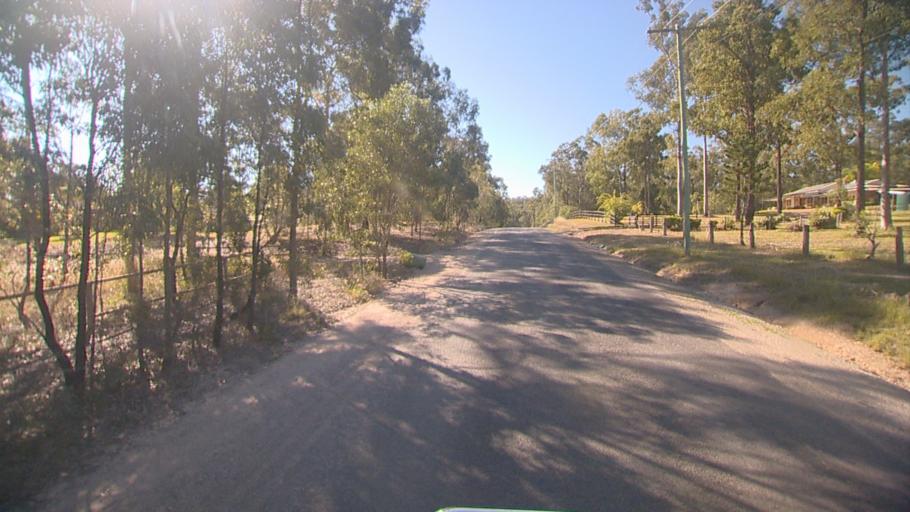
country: AU
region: Queensland
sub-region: Logan
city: Windaroo
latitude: -27.7568
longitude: 153.1511
